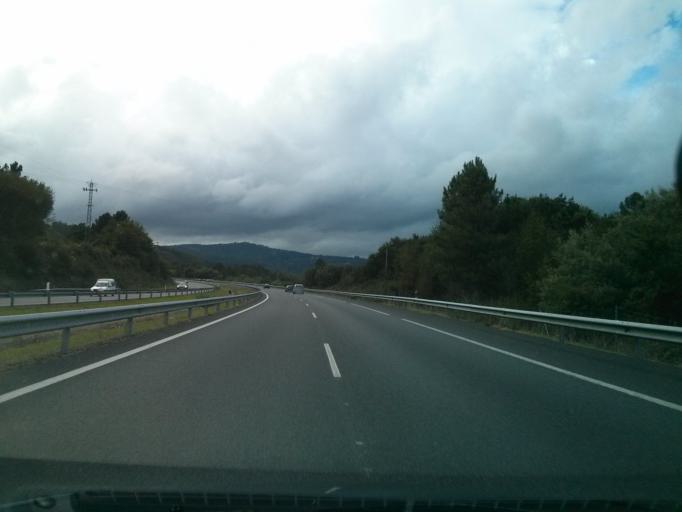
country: ES
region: Galicia
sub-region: Provincia de Ourense
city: Toen
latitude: 42.3338
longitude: -7.9677
